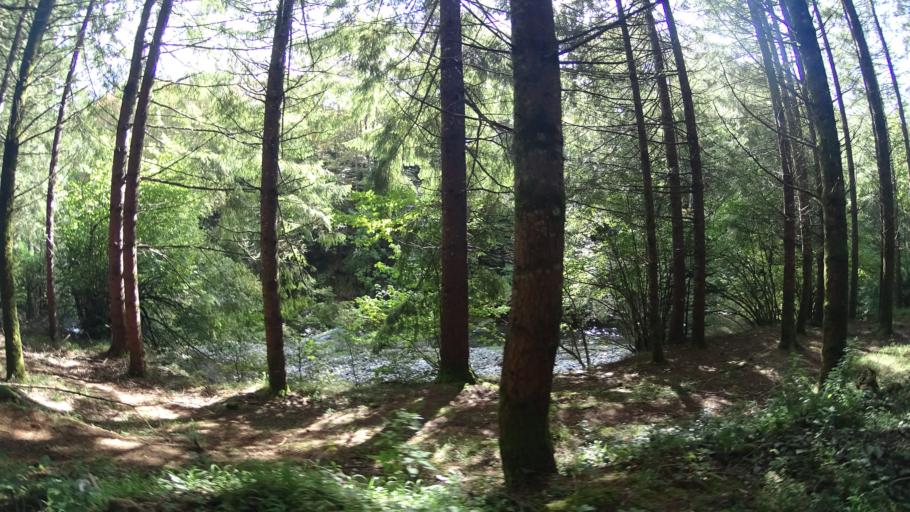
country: ES
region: Navarre
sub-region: Provincia de Navarra
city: Oronz
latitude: 42.9904
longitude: -1.1054
